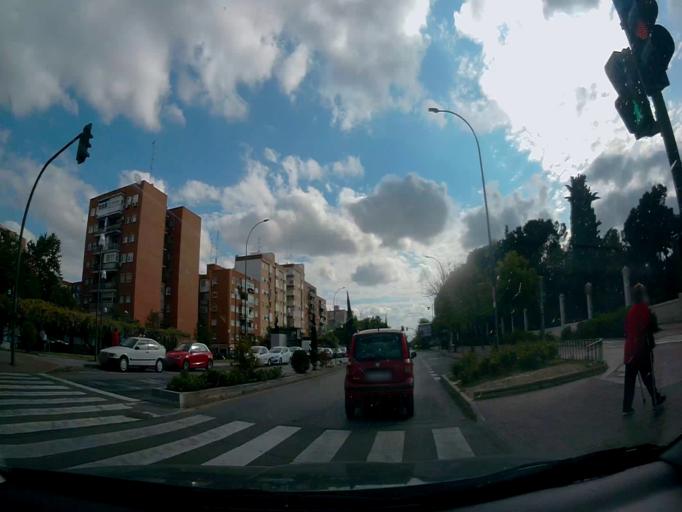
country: ES
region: Madrid
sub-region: Provincia de Madrid
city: Mostoles
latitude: 40.3240
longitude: -3.8714
